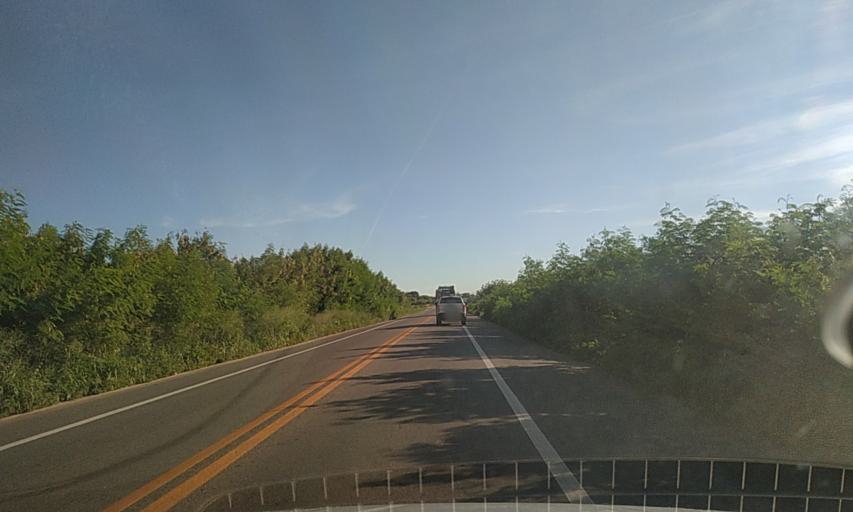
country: BR
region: Rio Grande do Norte
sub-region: Mossoro
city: Mossoro
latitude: -5.1951
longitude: -37.3146
